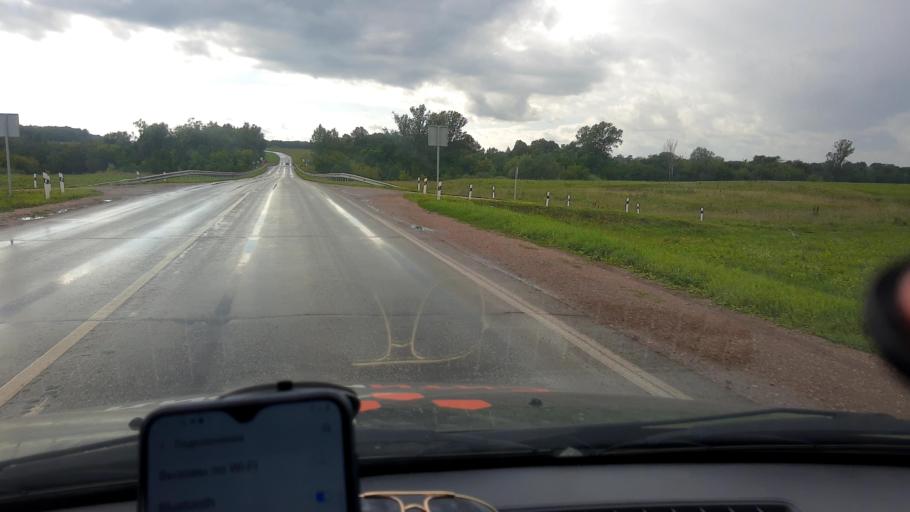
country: RU
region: Bashkortostan
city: Karmaskaly
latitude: 53.9301
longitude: 56.4172
